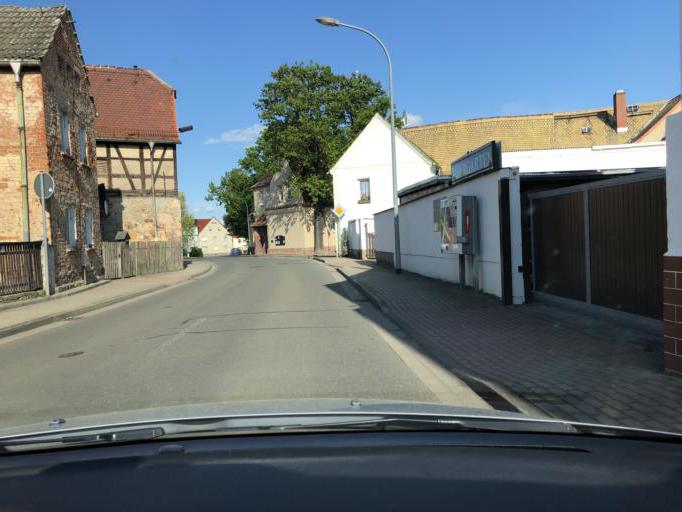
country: DE
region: Saxony
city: Regis-Breitingen
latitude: 51.0860
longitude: 12.4301
